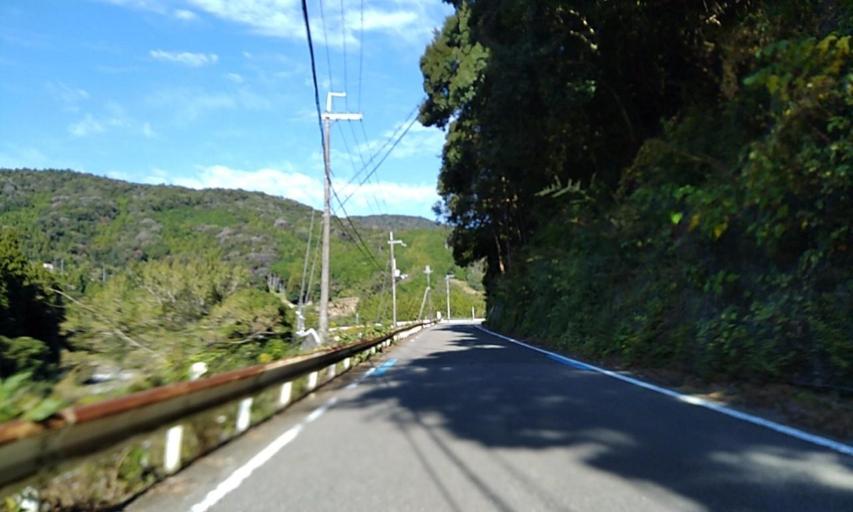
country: JP
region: Wakayama
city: Kainan
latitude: 34.0501
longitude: 135.3100
